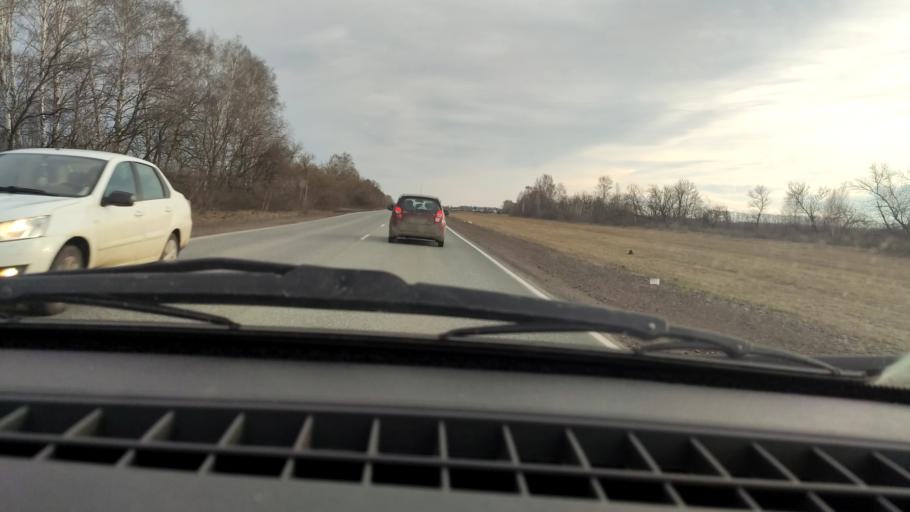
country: RU
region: Bashkortostan
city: Chishmy
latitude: 54.4137
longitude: 55.2235
